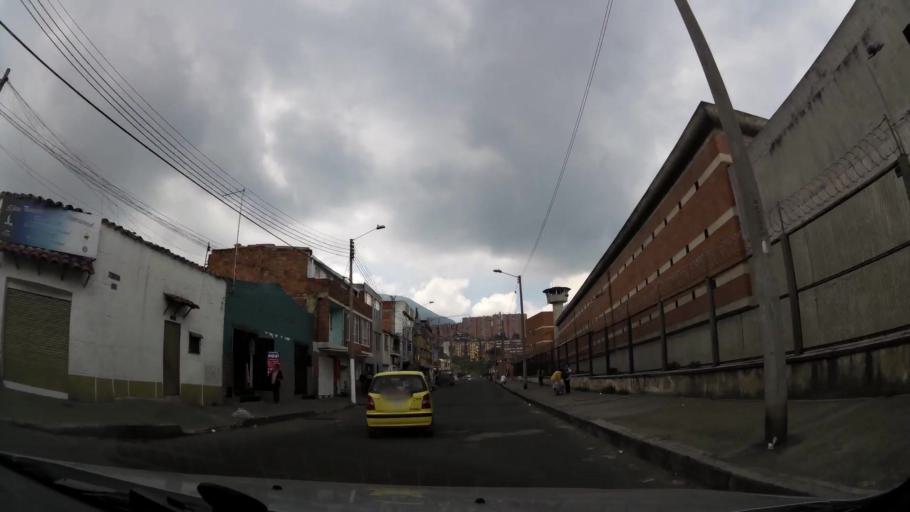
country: CO
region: Bogota D.C.
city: Bogota
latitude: 4.5862
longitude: -74.0850
